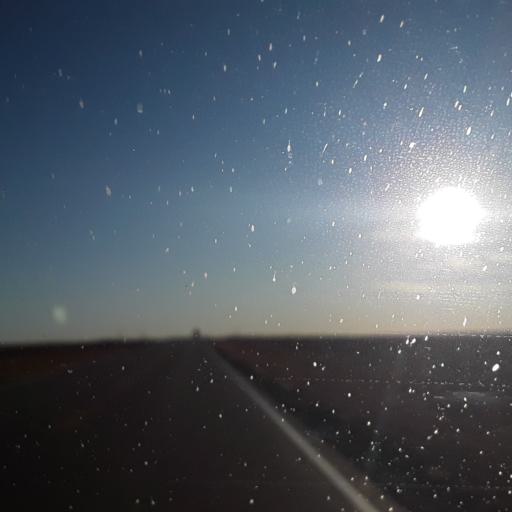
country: US
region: Kansas
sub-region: Wallace County
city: Sharon Springs
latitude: 38.9616
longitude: -101.7408
